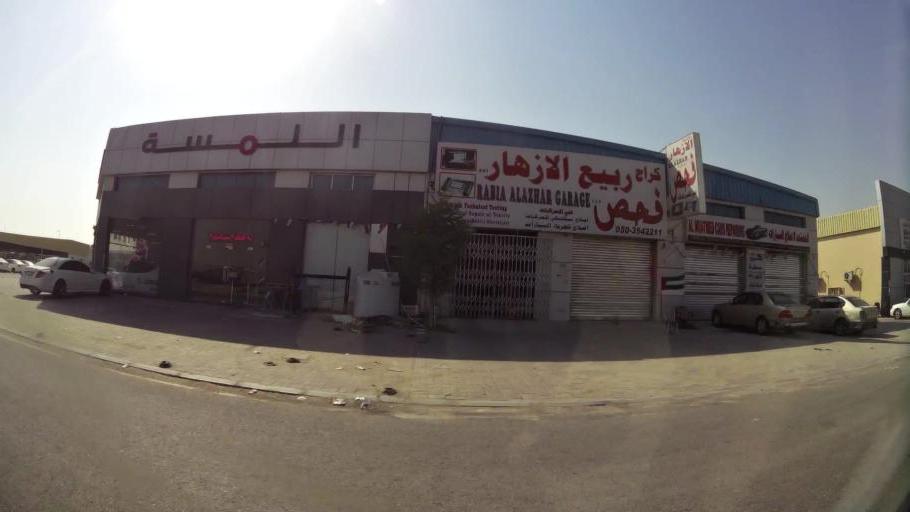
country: AE
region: Ajman
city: Ajman
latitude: 25.4388
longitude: 55.5108
